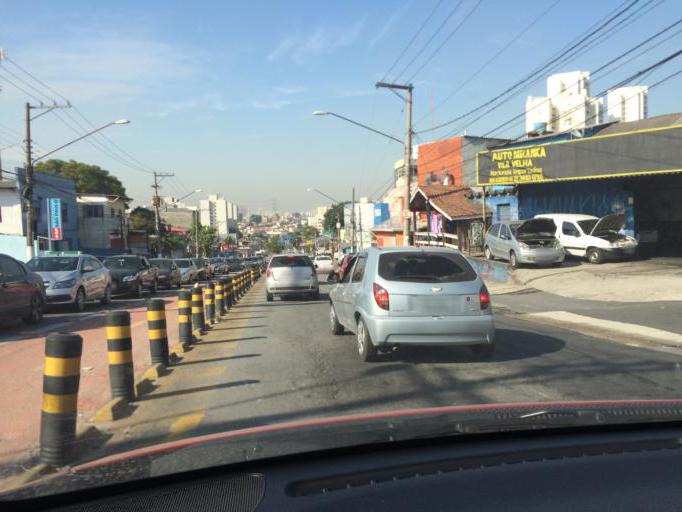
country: BR
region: Sao Paulo
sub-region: Osasco
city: Osasco
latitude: -23.5493
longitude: -46.7585
